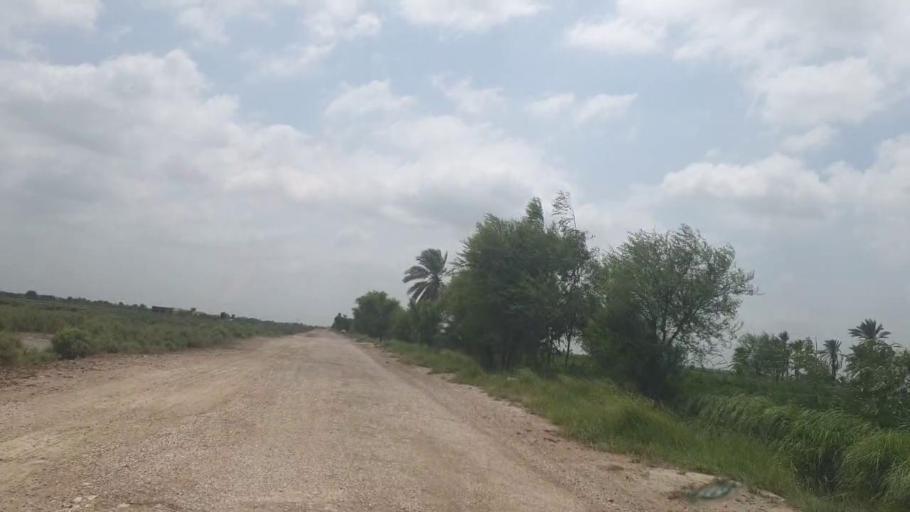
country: PK
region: Sindh
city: Tando Mittha Khan
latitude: 25.8873
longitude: 69.1558
